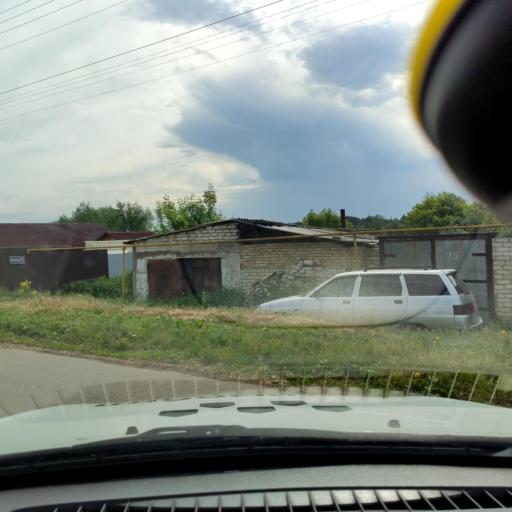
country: RU
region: Samara
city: Zhigulevsk
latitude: 53.5459
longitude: 49.5286
